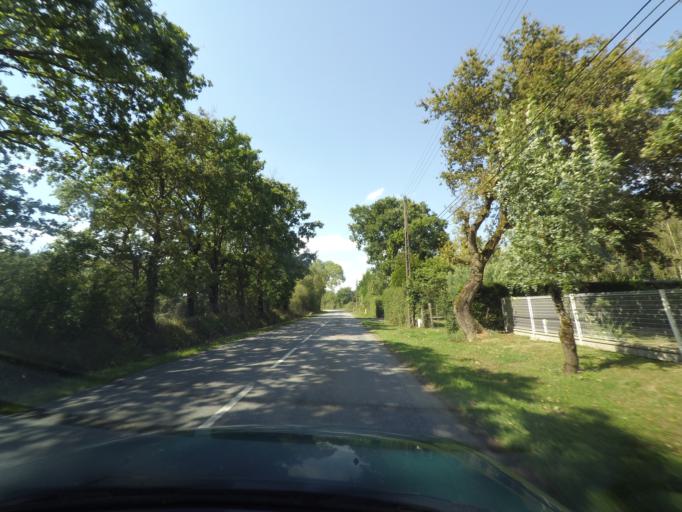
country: FR
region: Pays de la Loire
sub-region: Departement de la Loire-Atlantique
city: Saint-Lumine-de-Coutais
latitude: 47.0692
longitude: -1.7732
